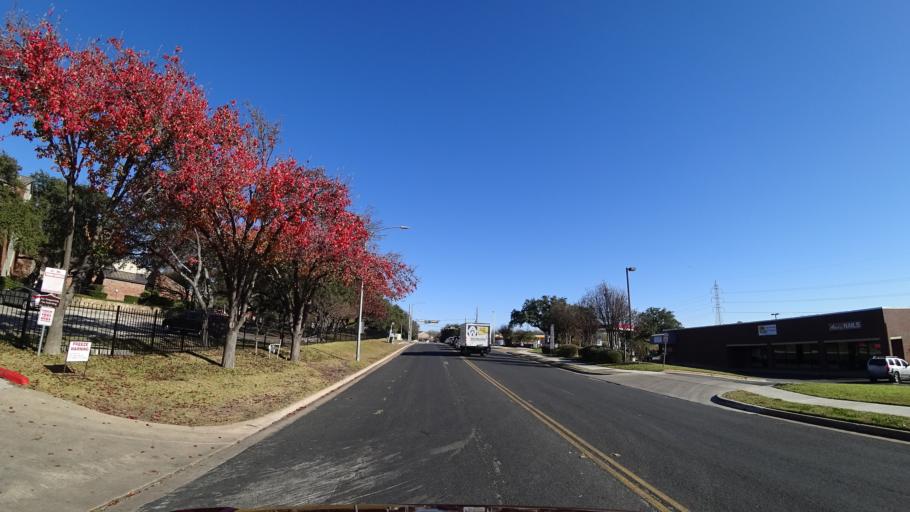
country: US
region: Texas
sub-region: Travis County
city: Wells Branch
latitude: 30.4086
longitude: -97.6981
